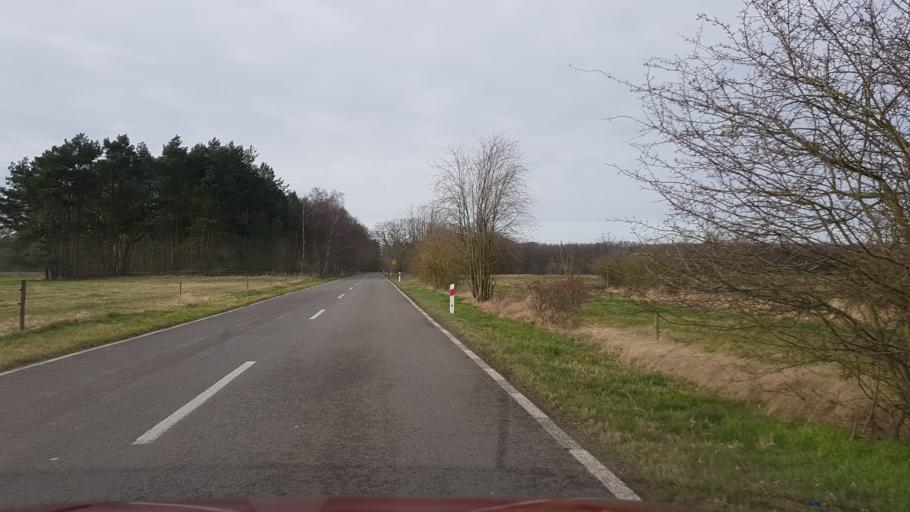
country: PL
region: West Pomeranian Voivodeship
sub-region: Powiat policki
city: Nowe Warpno
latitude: 53.6969
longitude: 14.3482
